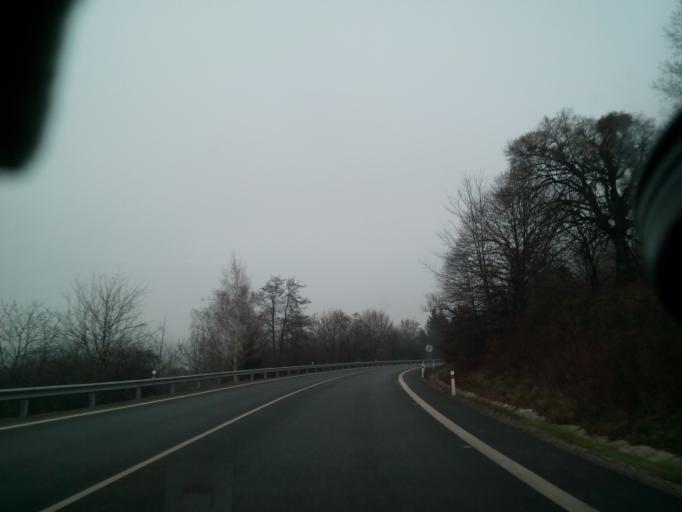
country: SK
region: Kosicky
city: Kosice
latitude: 48.7397
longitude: 21.3636
